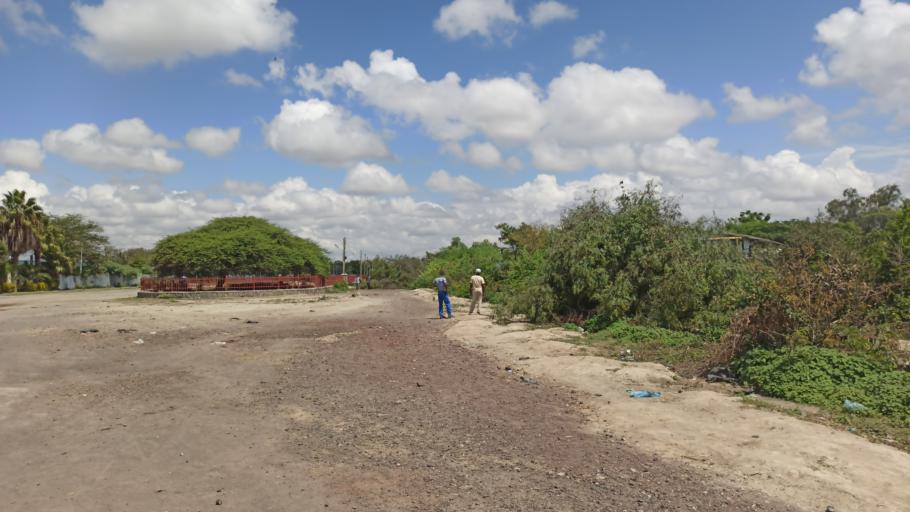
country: ET
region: Oromiya
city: Ziway
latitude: 7.9256
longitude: 38.7237
